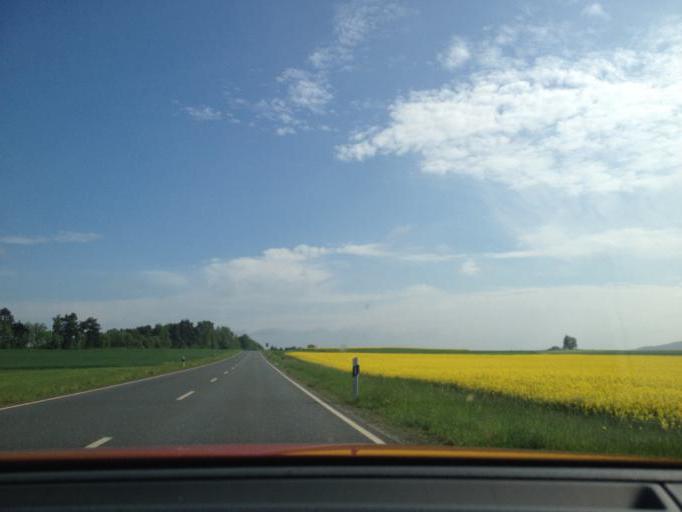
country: DE
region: Bavaria
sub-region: Upper Palatinate
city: Waldershof
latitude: 49.9670
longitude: 12.0406
